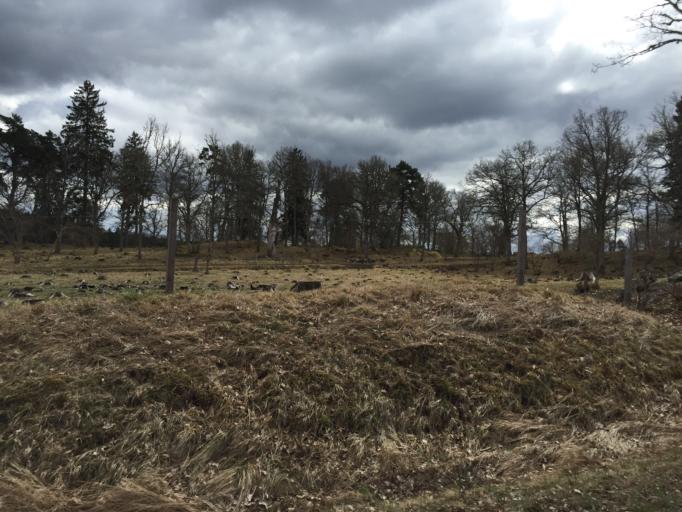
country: SE
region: Soedermanland
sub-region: Nykopings Kommun
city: Nykoping
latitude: 58.9855
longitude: 16.9473
